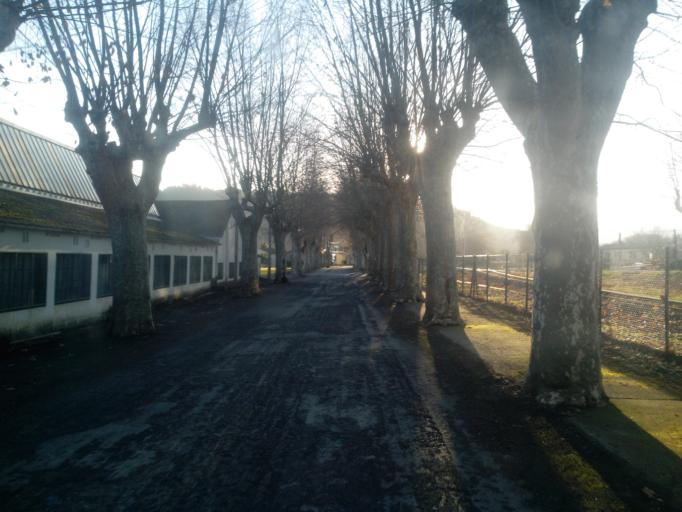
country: FR
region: Languedoc-Roussillon
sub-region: Departement de l'Aude
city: Couiza
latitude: 42.9438
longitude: 2.2509
